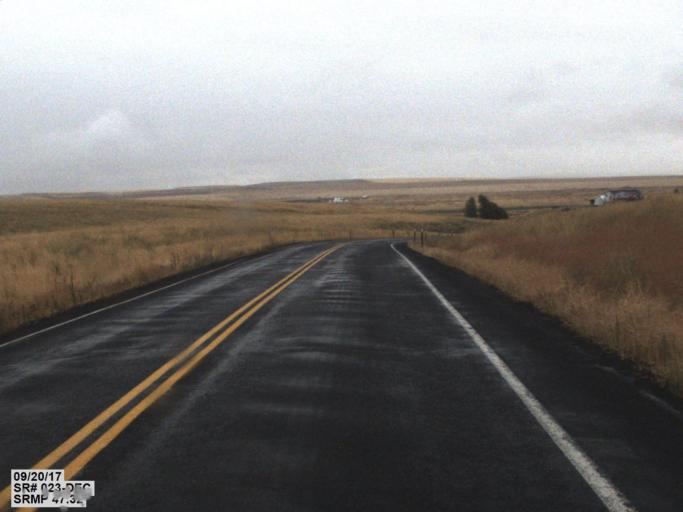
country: US
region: Washington
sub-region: Lincoln County
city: Davenport
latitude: 47.3441
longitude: -118.0100
